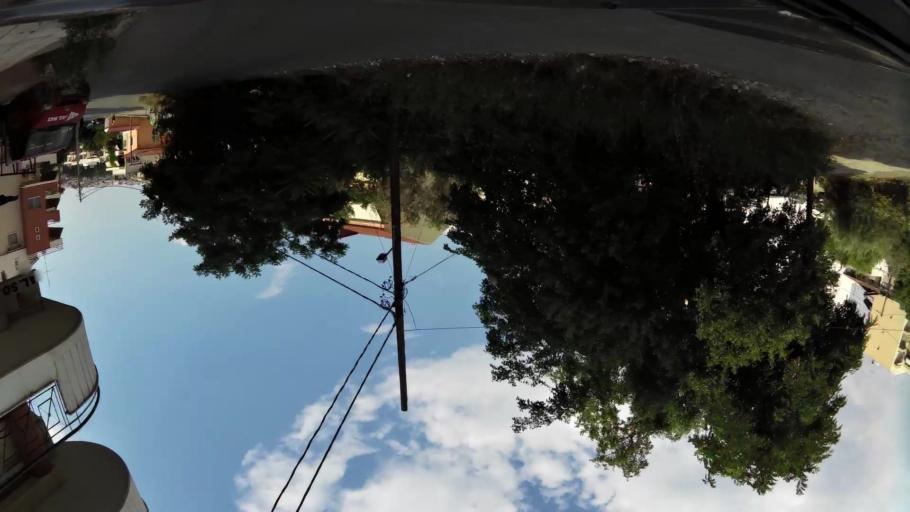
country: GR
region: Central Macedonia
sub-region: Nomos Thessalonikis
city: Sykies
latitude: 40.6579
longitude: 22.9620
